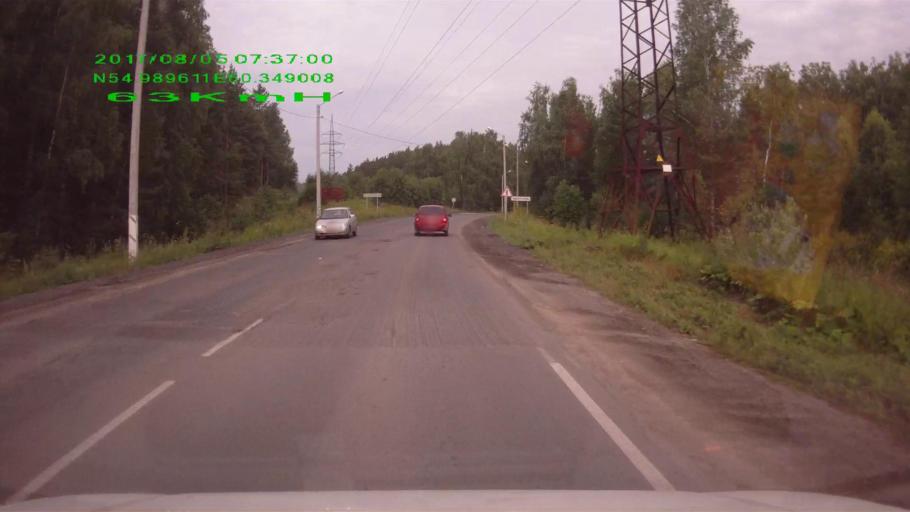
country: RU
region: Chelyabinsk
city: Chebarkul'
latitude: 54.9897
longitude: 60.3486
